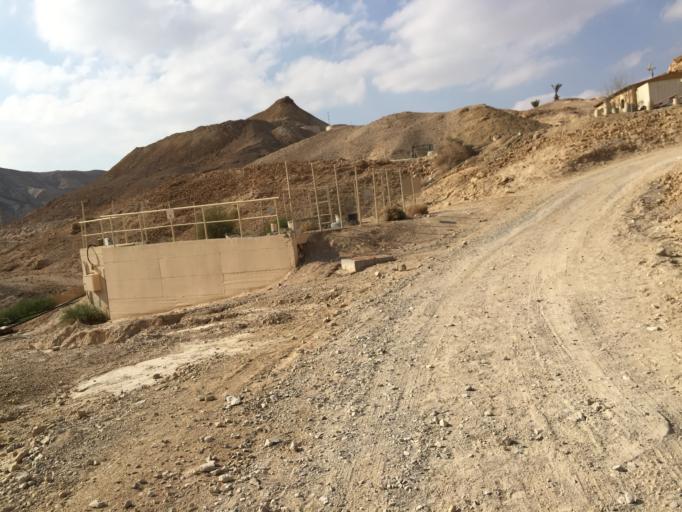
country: IL
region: Southern District
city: `En Boqeq
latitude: 31.3174
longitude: 35.3492
